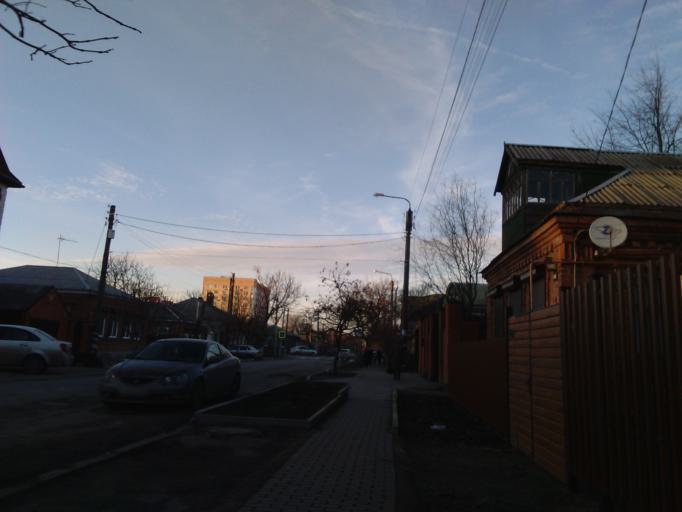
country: RU
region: Rostov
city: Bataysk
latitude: 47.1408
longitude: 39.7448
